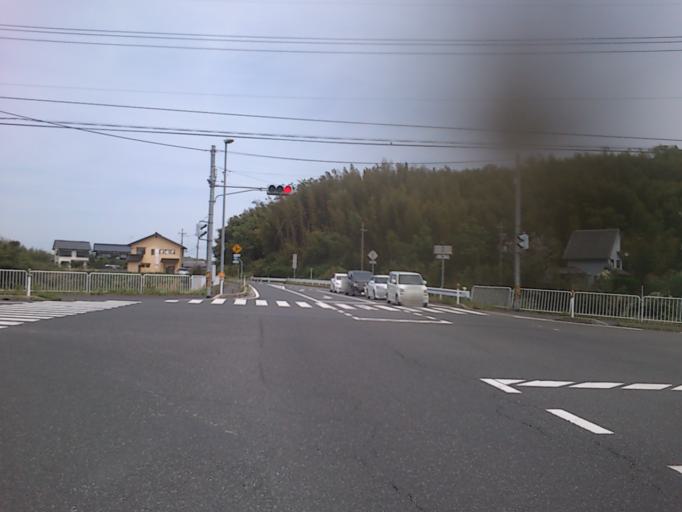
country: JP
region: Kyoto
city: Miyazu
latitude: 35.6308
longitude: 135.0813
